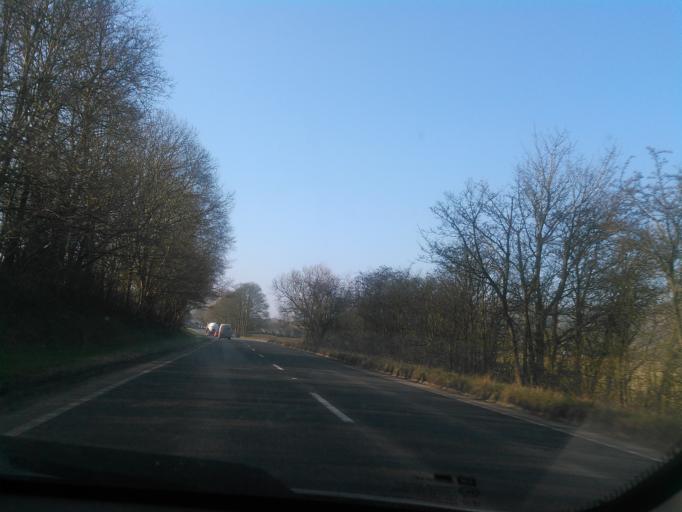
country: GB
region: England
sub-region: Shropshire
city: Church Stretton
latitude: 52.5564
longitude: -2.7857
